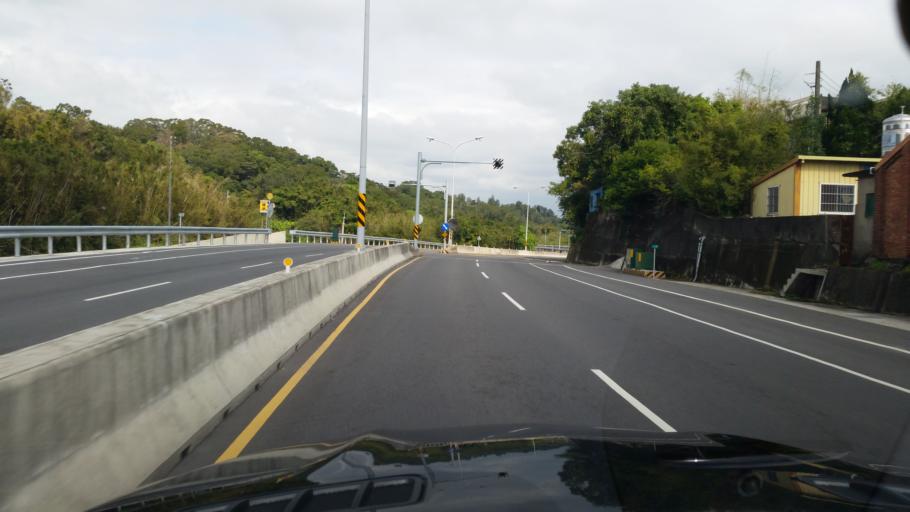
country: TW
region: Taiwan
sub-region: Miaoli
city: Miaoli
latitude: 24.6316
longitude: 120.8558
